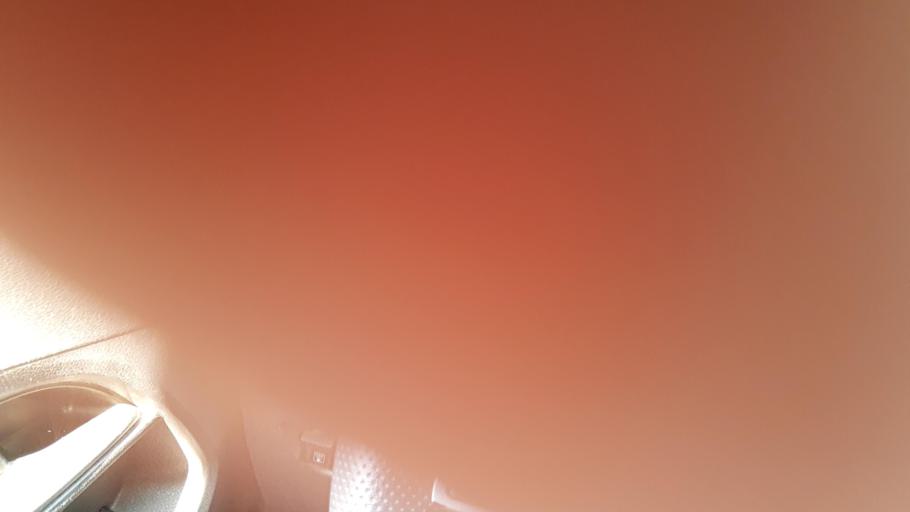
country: RU
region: Bashkortostan
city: Kabakovo
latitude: 54.6525
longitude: 56.0921
